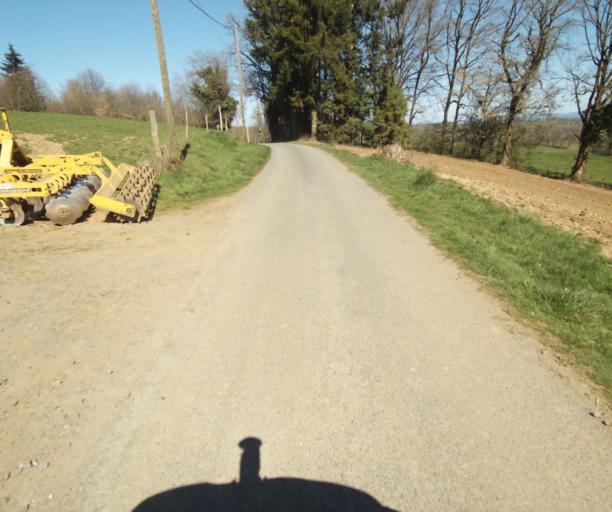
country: FR
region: Limousin
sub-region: Departement de la Correze
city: Uzerche
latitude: 45.3928
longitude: 1.6076
